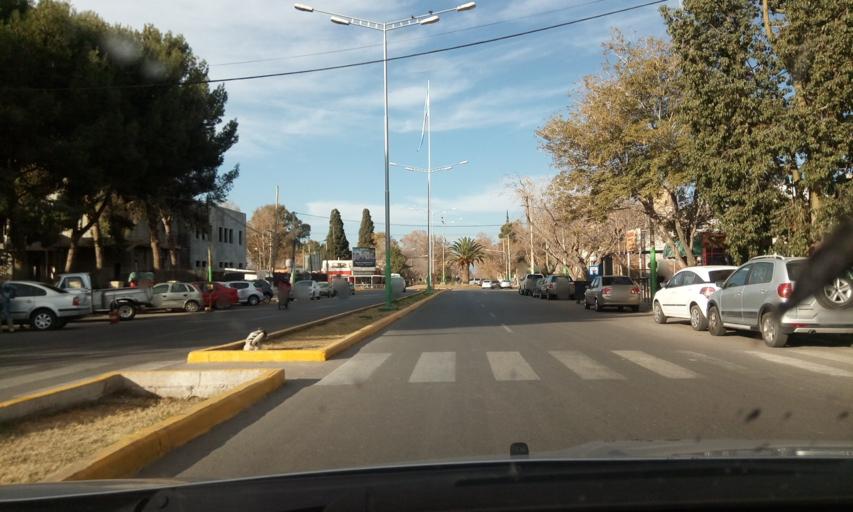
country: AR
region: San Juan
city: San Juan
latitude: -31.5307
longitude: -68.5957
